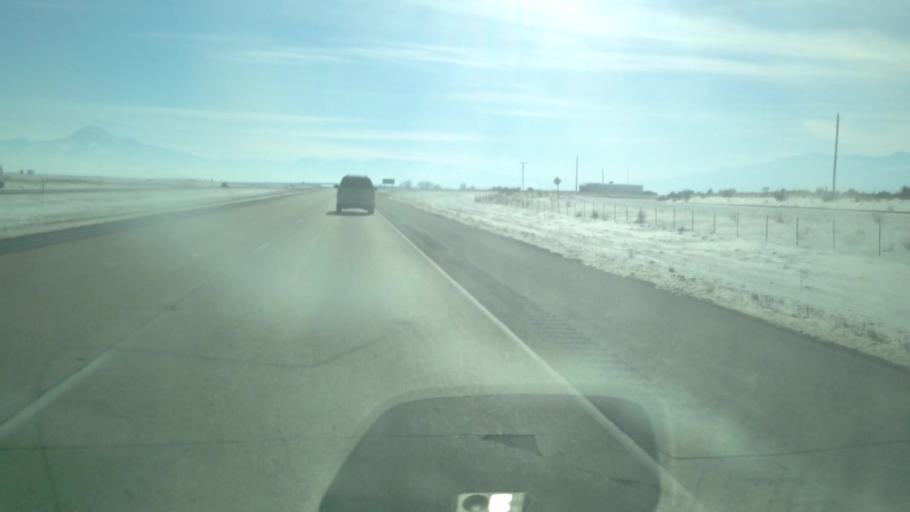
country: US
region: Idaho
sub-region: Oneida County
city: Malad City
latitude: 42.4915
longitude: -112.1698
